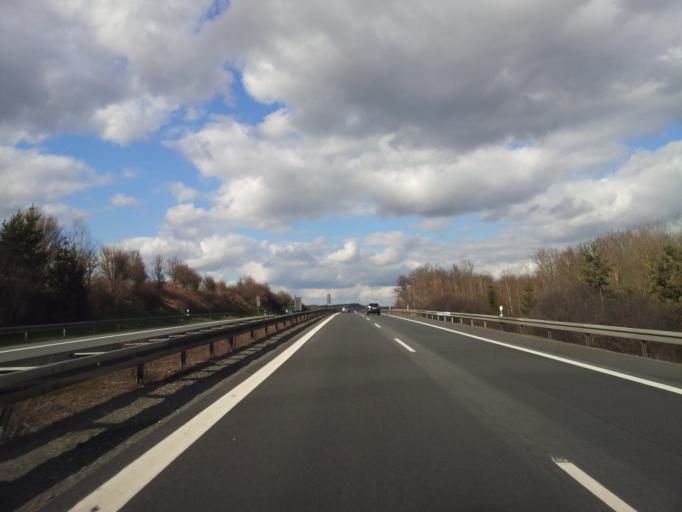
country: DE
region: Saxony
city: Theuma
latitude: 50.4773
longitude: 12.1843
